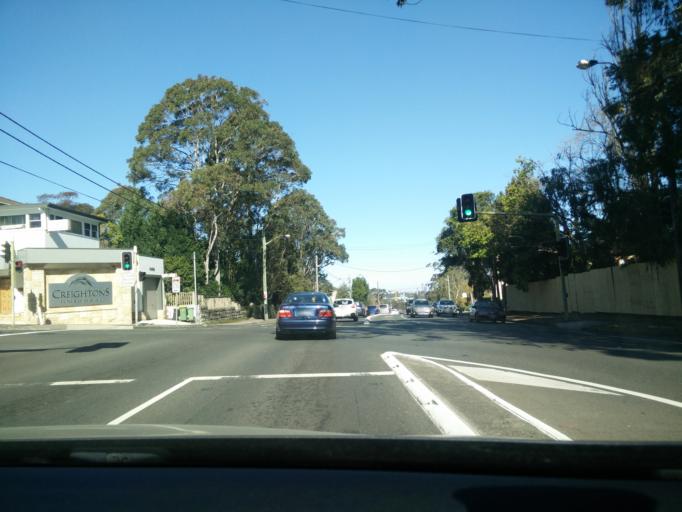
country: AU
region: New South Wales
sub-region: City of Sydney
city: Pymble
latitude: -33.7416
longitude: 151.1388
